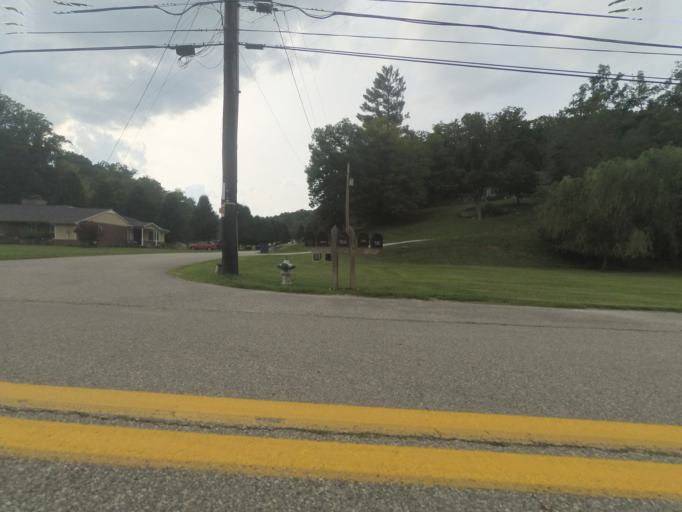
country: US
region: West Virginia
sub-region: Cabell County
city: Huntington
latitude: 38.3859
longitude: -82.4042
